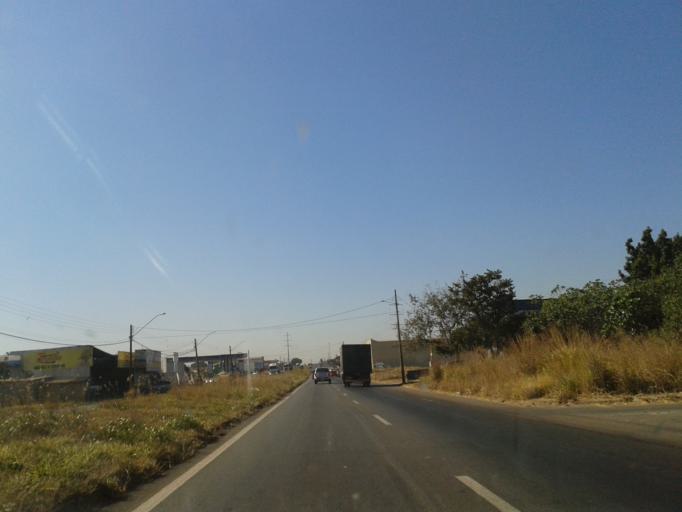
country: BR
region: Goias
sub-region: Aparecida De Goiania
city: Aparecida de Goiania
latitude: -16.7743
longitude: -49.3028
